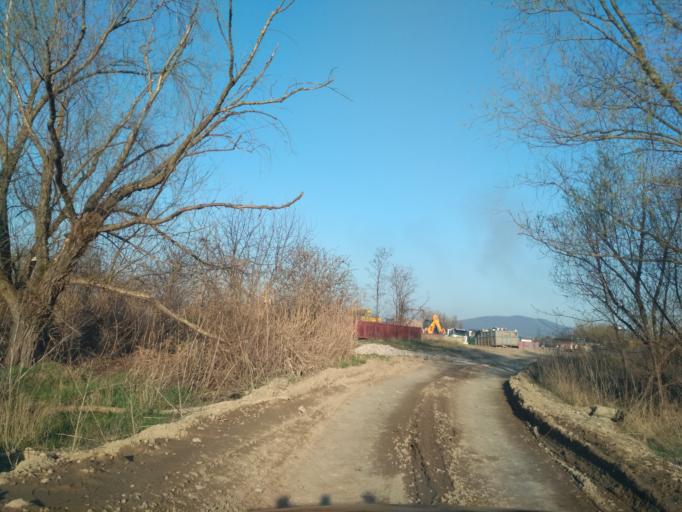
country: SK
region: Kosicky
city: Kosice
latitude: 48.6688
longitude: 21.3039
